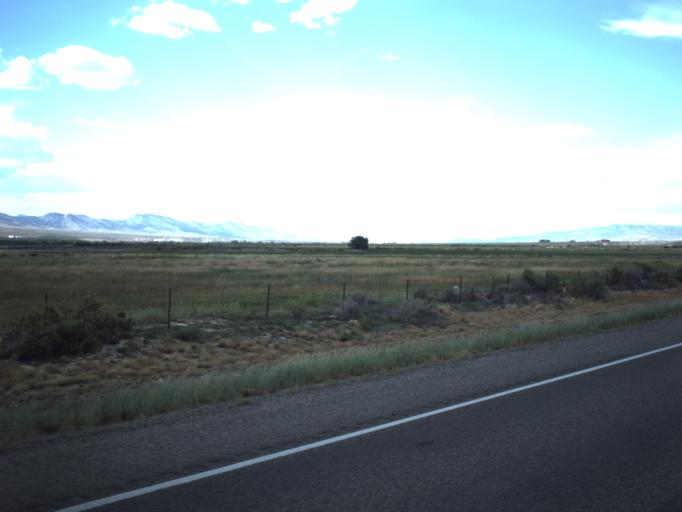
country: US
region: Utah
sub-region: Sevier County
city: Salina
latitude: 39.0016
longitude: -111.8405
